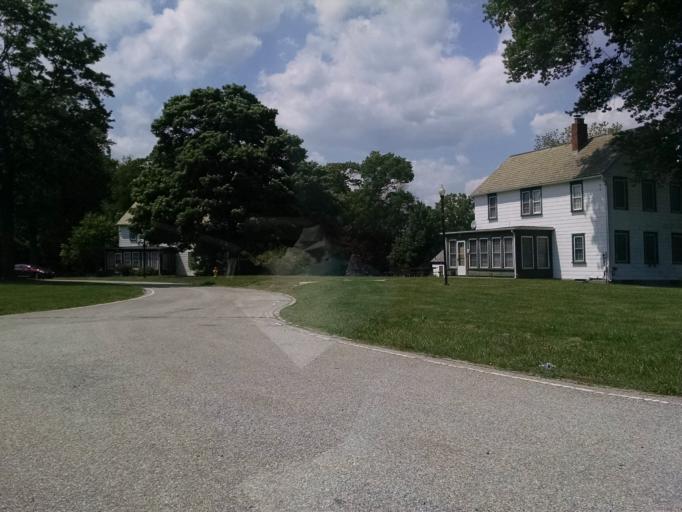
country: US
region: New York
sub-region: Richmond County
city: Staten Island
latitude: 40.5715
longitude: -74.1013
